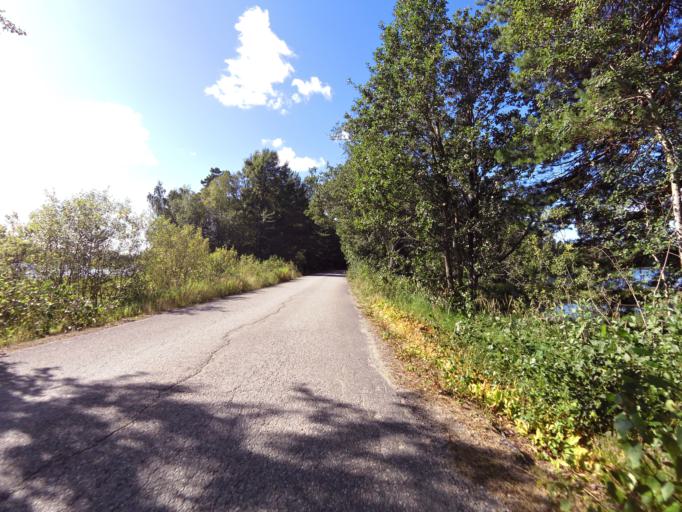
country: SE
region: Gaevleborg
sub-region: Gavle Kommun
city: Valbo
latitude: 60.7688
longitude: 16.9409
